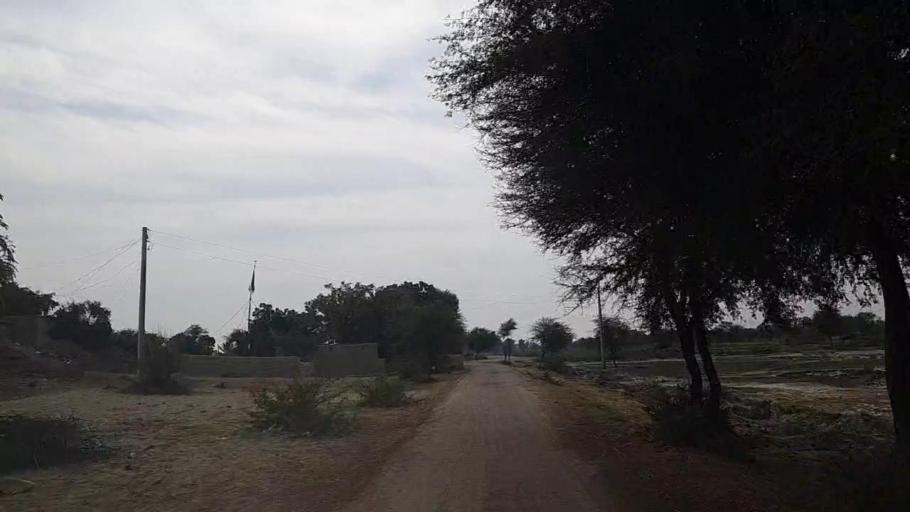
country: PK
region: Sindh
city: Daur
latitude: 26.4322
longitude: 68.4720
